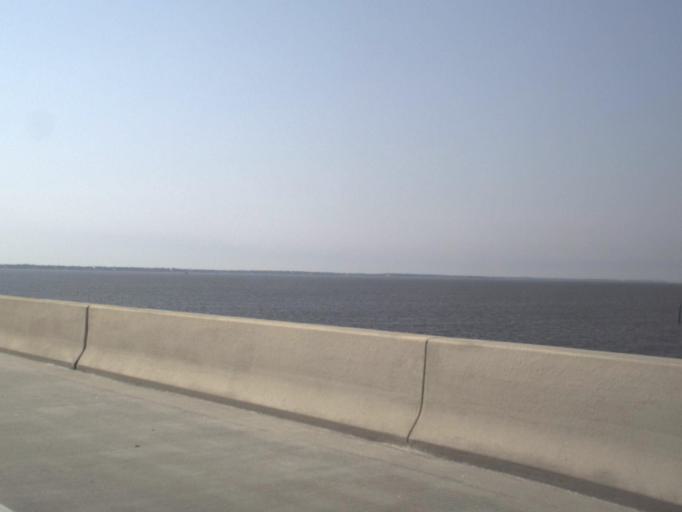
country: US
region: Florida
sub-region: Franklin County
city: Eastpoint
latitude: 29.6955
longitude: -84.8890
